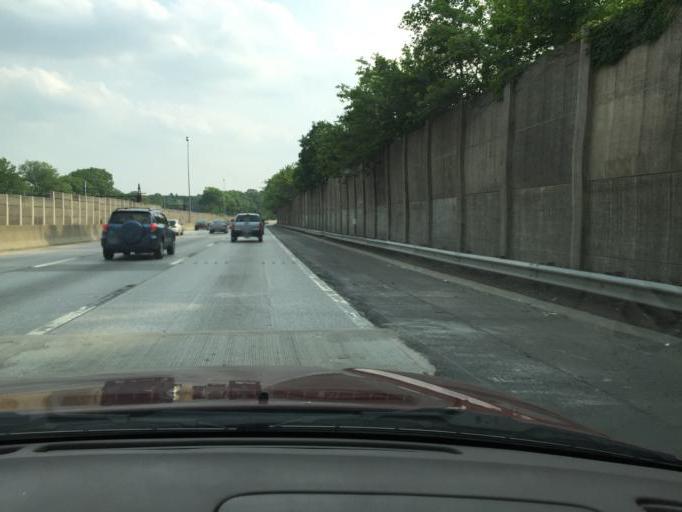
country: US
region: New York
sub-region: Westchester County
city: Pelham Manor
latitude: 40.8905
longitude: -73.8009
